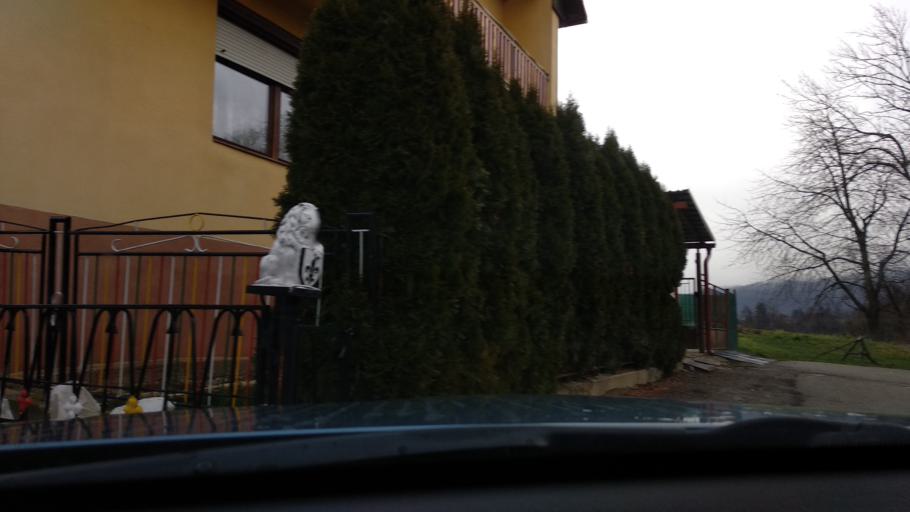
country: SK
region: Trenciansky
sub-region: Okres Trencin
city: Trencin
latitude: 48.8462
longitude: 18.0459
